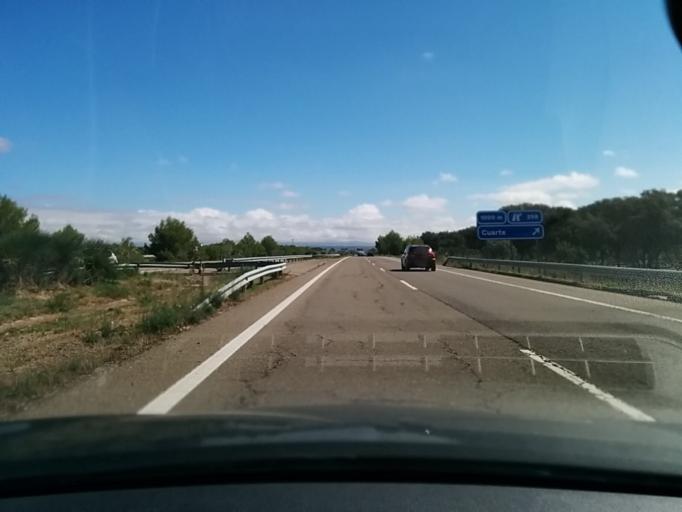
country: ES
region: Aragon
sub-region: Provincia de Huesca
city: Huesca
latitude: 42.1070
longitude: -0.4559
